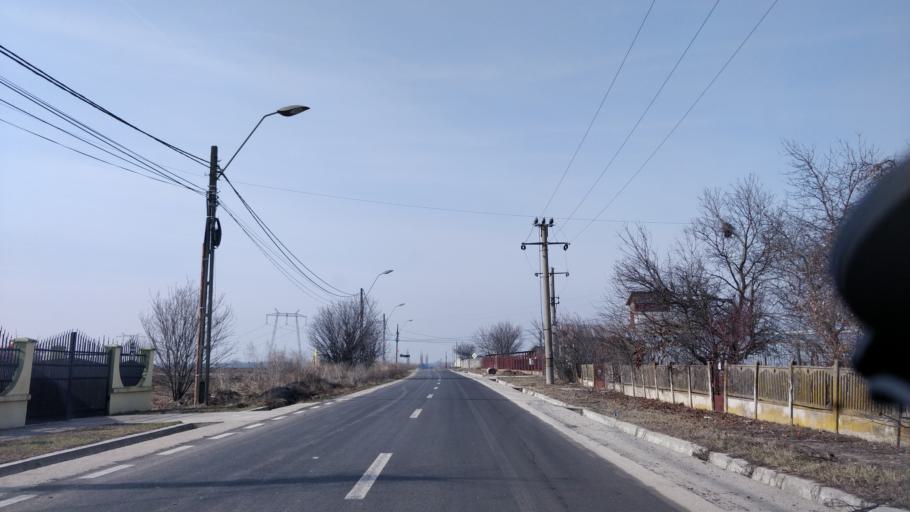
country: RO
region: Giurgiu
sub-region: Comuna Bolintin Deal
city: Bolintin Deal
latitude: 44.4620
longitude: 25.8039
